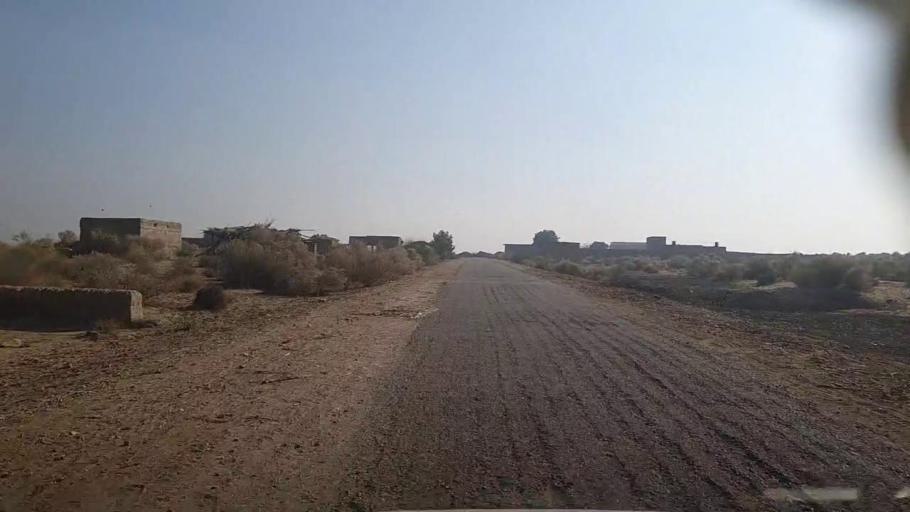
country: PK
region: Sindh
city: Kandiari
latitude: 26.8260
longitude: 68.4891
